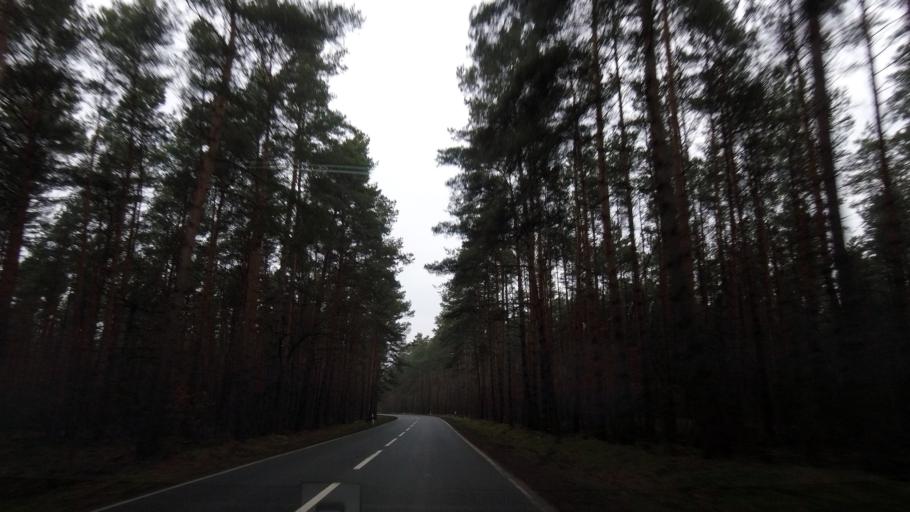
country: DE
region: Brandenburg
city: Niedergorsdorf
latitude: 52.0288
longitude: 12.9484
